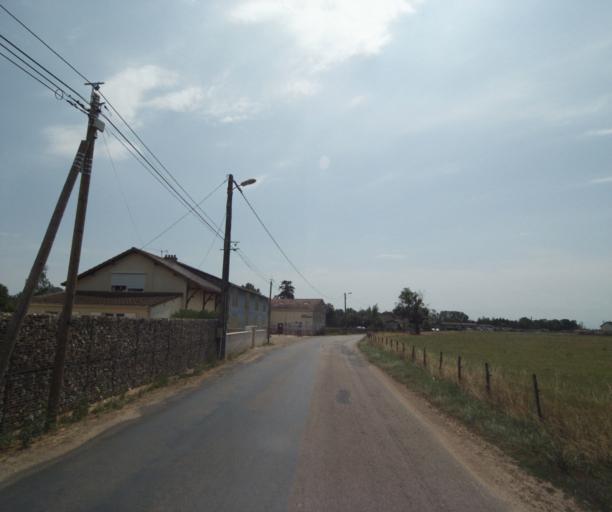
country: FR
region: Bourgogne
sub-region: Departement de Saone-et-Loire
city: Gueugnon
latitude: 46.5913
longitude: 4.0534
